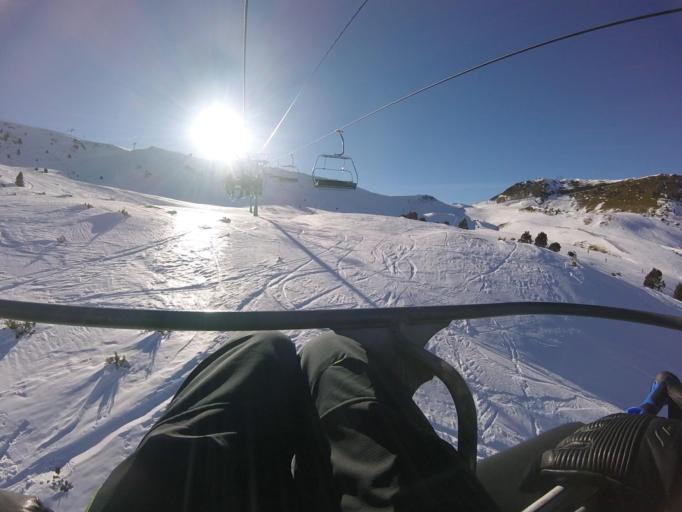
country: AD
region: Canillo
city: El Tarter
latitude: 42.5503
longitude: 1.6607
